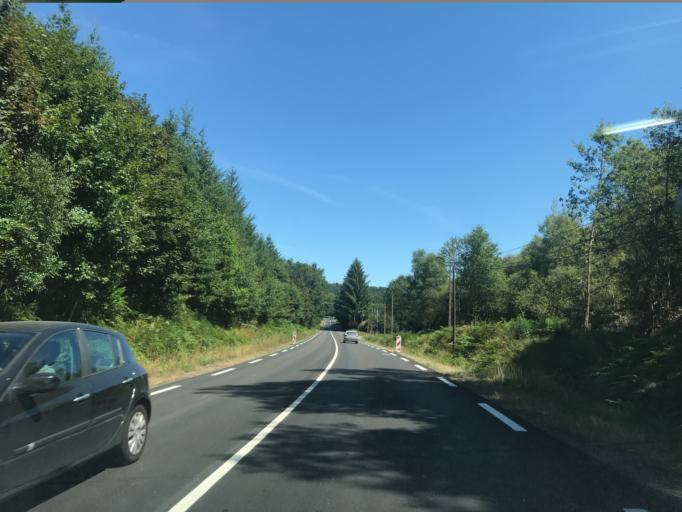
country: FR
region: Limousin
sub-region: Departement de la Correze
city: Egletons
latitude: 45.3851
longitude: 2.0228
